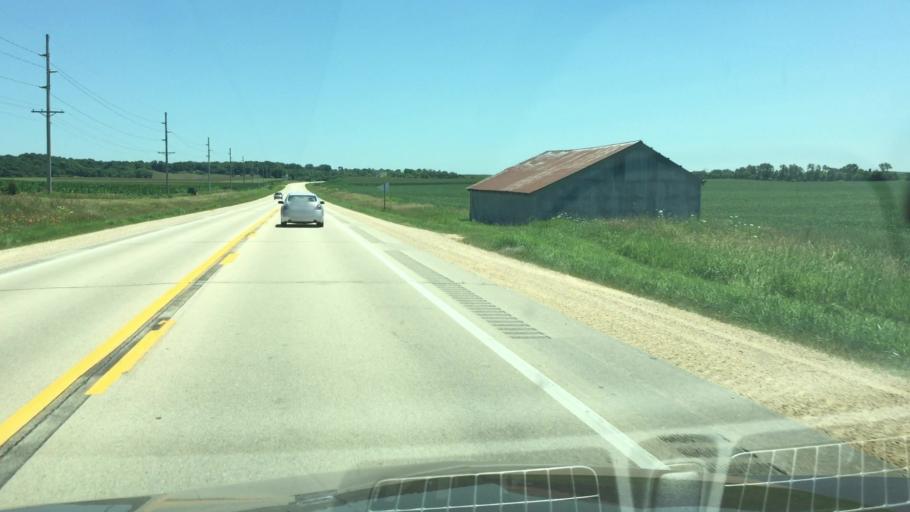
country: US
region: Iowa
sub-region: Jackson County
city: Maquoketa
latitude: 42.0663
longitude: -90.7761
